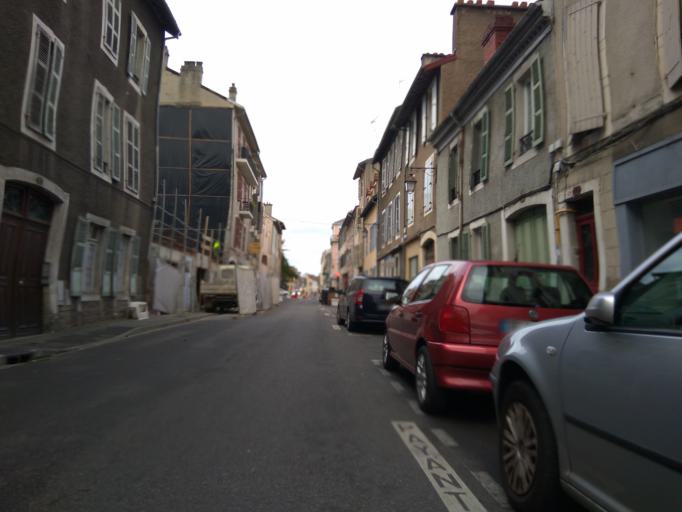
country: FR
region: Aquitaine
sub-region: Departement des Pyrenees-Atlantiques
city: Pau
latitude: 43.2998
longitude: -0.3642
